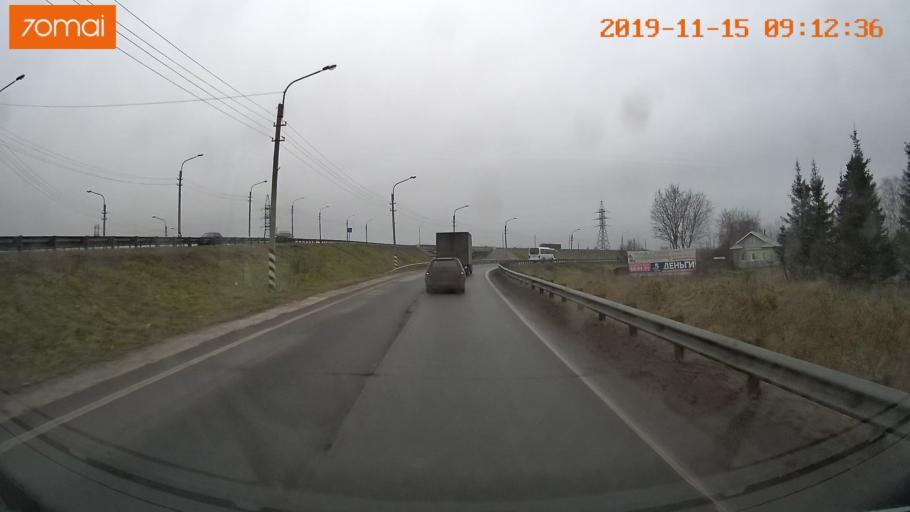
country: RU
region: Vologda
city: Tonshalovo
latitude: 59.2095
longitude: 37.9358
